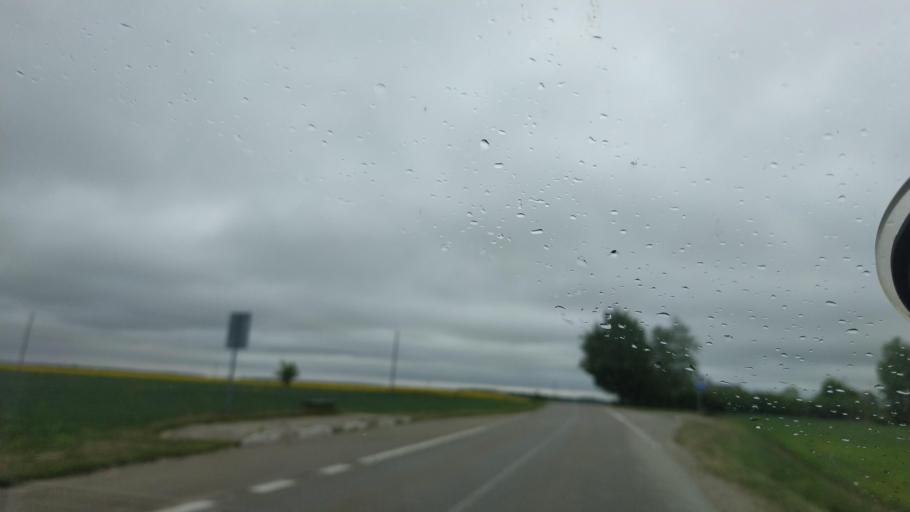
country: LT
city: Vabalninkas
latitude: 55.9916
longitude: 24.6960
